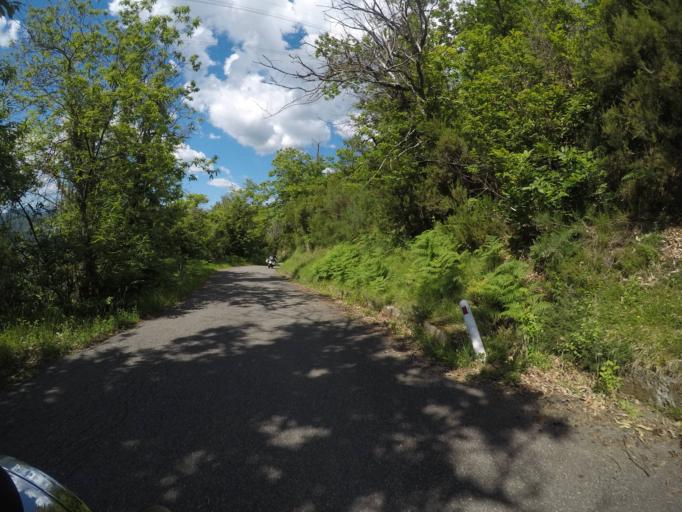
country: IT
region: Tuscany
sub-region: Provincia di Massa-Carrara
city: Casola in Lunigiana
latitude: 44.1766
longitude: 10.1554
